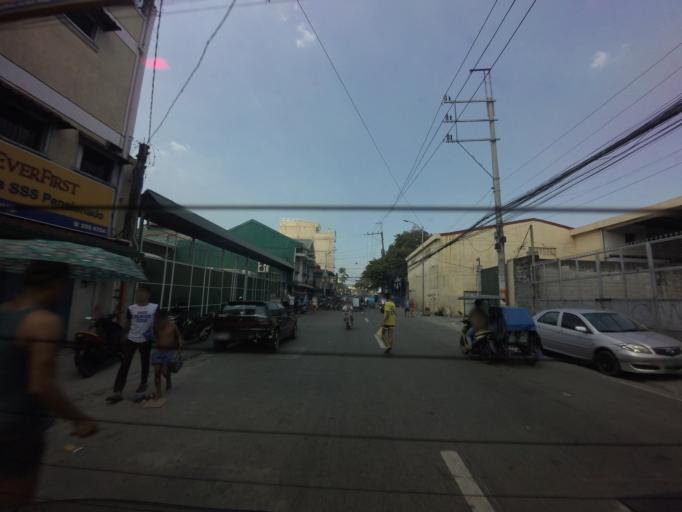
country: PH
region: Metro Manila
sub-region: City of Manila
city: Manila
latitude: 14.6180
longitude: 120.9682
